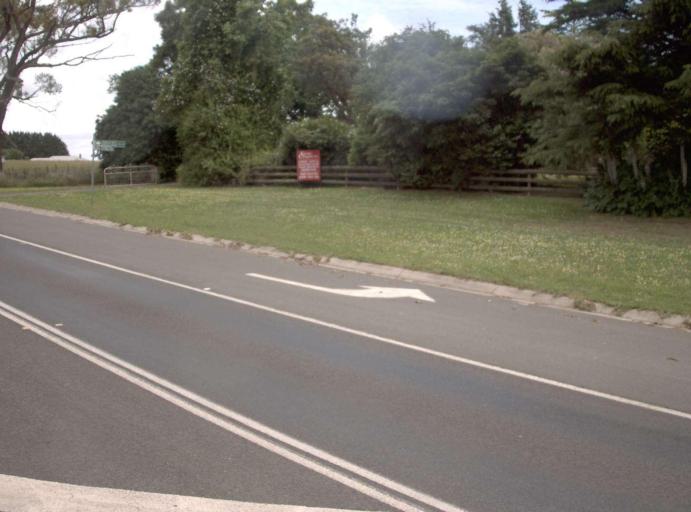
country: AU
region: Victoria
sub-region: Baw Baw
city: Warragul
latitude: -38.1117
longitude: 145.8416
